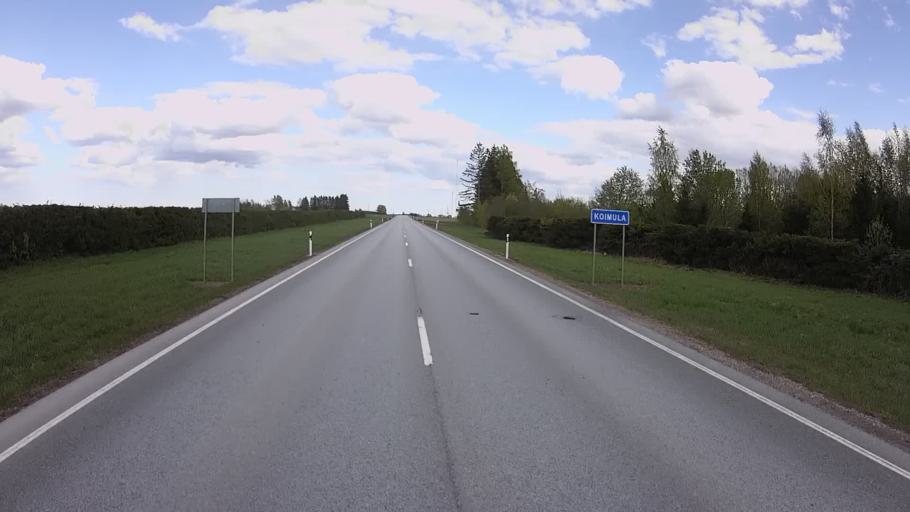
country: EE
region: Jogevamaa
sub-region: Jogeva linn
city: Jogeva
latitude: 58.8248
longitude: 26.6166
